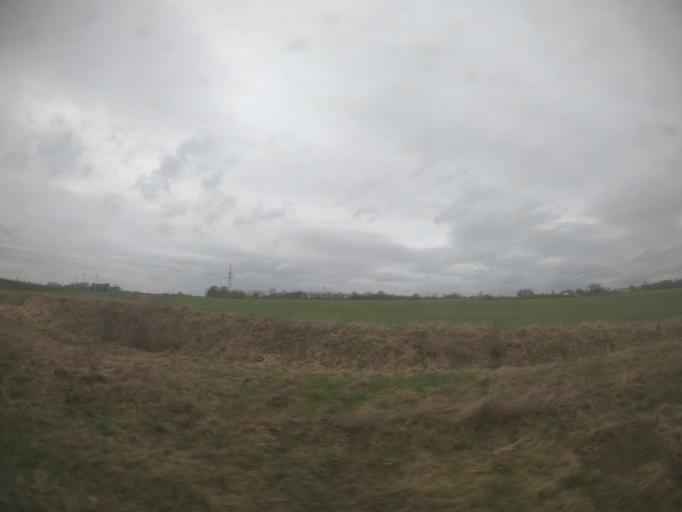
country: PL
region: West Pomeranian Voivodeship
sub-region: Powiat szczecinecki
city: Szczecinek
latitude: 53.7075
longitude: 16.7295
